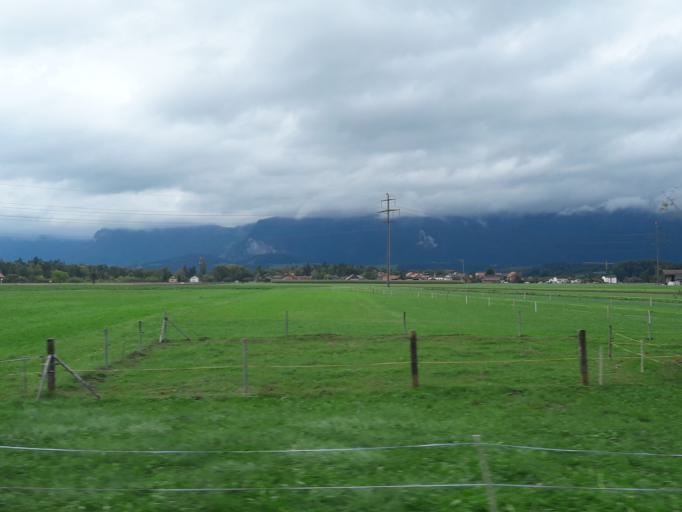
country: CH
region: Bern
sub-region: Thun District
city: Uetendorf
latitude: 46.7733
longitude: 7.5921
